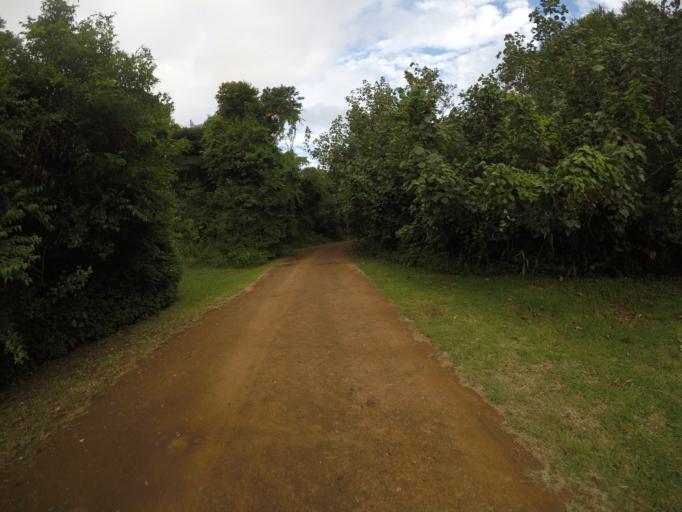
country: ZA
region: KwaZulu-Natal
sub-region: uMkhanyakude District Municipality
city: Mtubatuba
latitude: -28.3877
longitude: 32.4060
